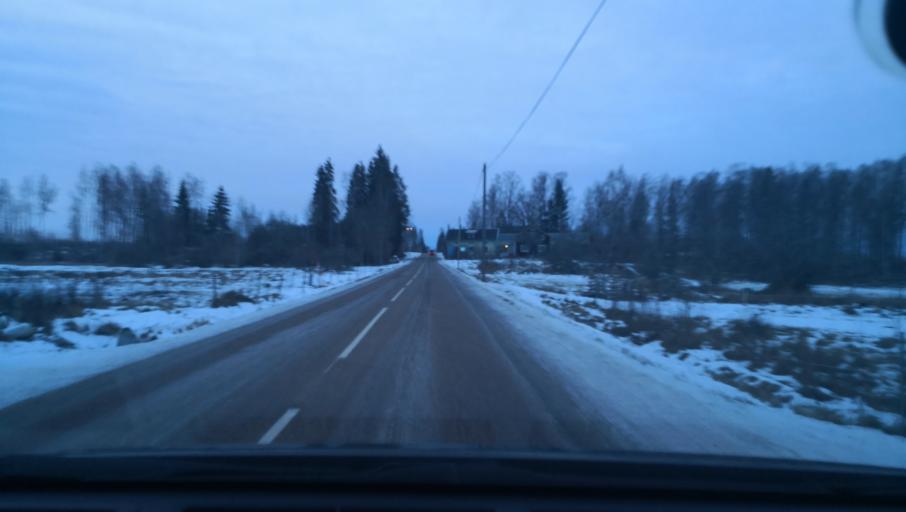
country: SE
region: Dalarna
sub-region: Avesta Kommun
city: Horndal
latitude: 60.1900
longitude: 16.4695
